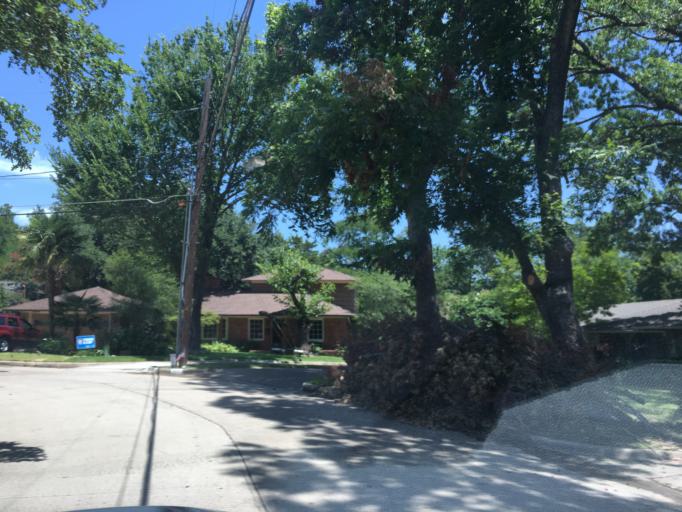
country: US
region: Texas
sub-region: Dallas County
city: Highland Park
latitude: 32.8377
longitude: -96.7456
